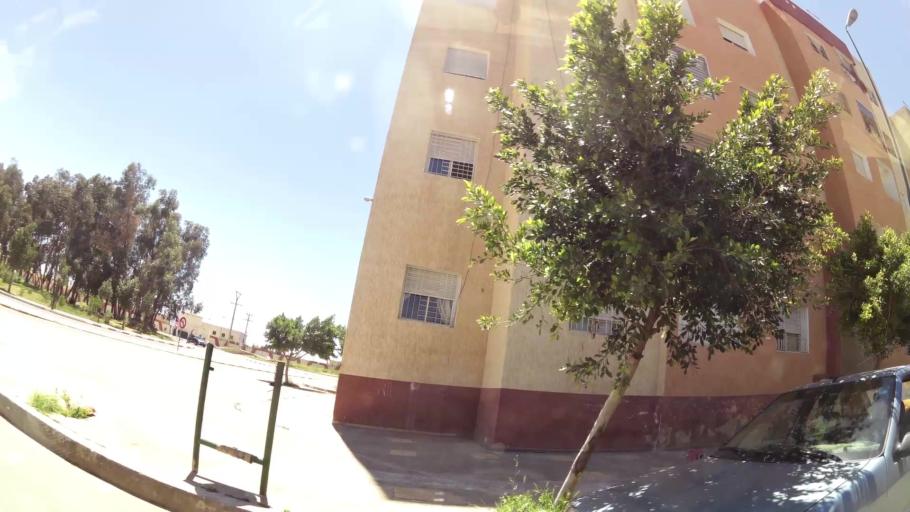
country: MA
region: Meknes-Tafilalet
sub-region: Meknes
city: Meknes
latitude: 33.8489
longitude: -5.5504
